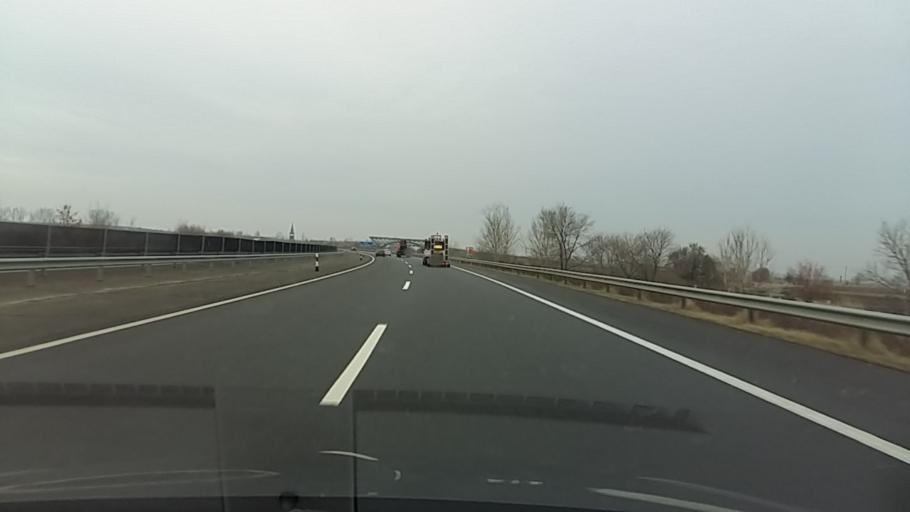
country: HU
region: Hajdu-Bihar
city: Polgar
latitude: 47.8385
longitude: 21.1522
